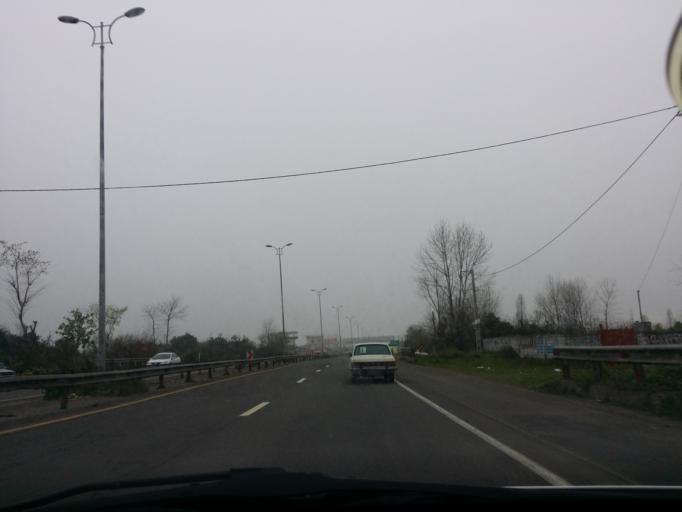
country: IR
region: Mazandaran
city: Tonekabon
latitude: 36.8204
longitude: 50.8479
